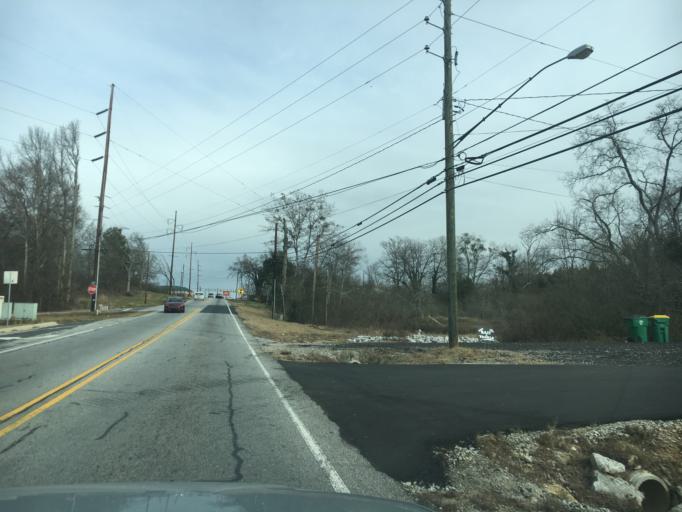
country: US
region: Georgia
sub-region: Barrow County
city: Winder
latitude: 33.9878
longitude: -83.7293
